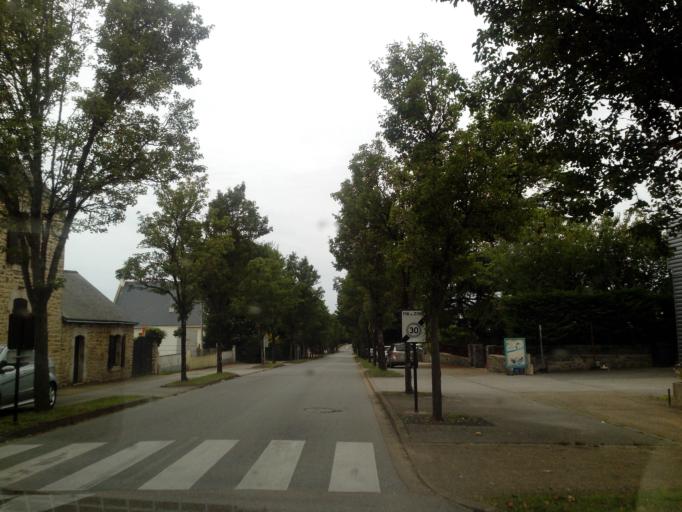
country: FR
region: Brittany
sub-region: Departement du Morbihan
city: Pont-Scorff
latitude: 47.8343
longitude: -3.4050
